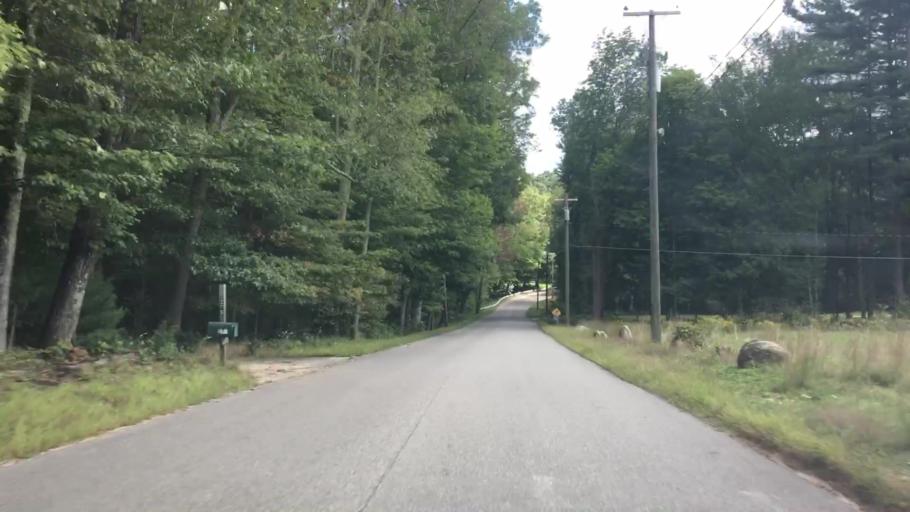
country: US
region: Connecticut
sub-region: Tolland County
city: Stafford Springs
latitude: 41.9186
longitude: -72.2176
